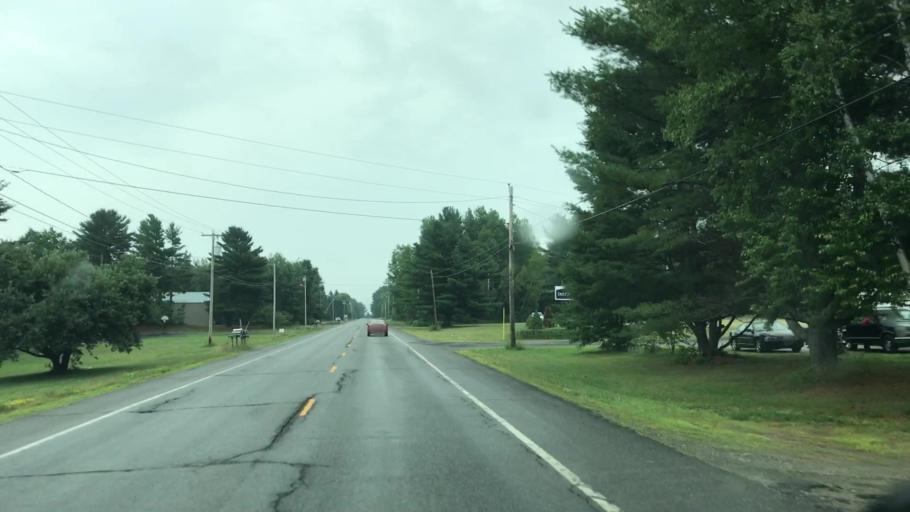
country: US
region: Maine
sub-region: Penobscot County
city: Lincoln
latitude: 45.3418
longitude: -68.5660
